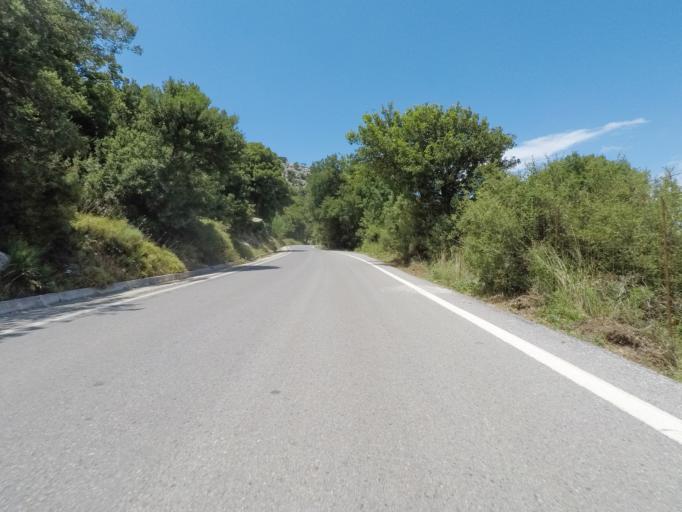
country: GR
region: Crete
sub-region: Nomos Irakleiou
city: Mokhos
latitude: 35.1727
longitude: 25.4369
